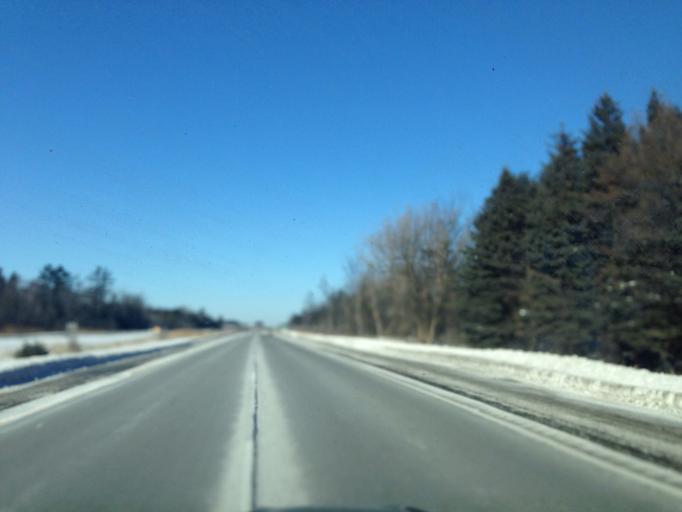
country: CA
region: Ontario
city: Ottawa
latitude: 45.3670
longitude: -75.5254
